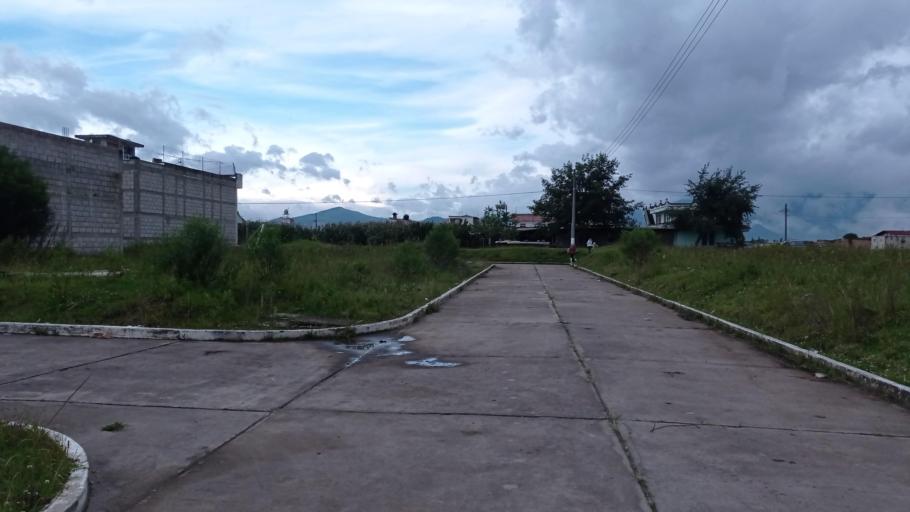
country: GT
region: Quetzaltenango
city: Olintepeque
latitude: 14.8643
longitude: -91.5083
